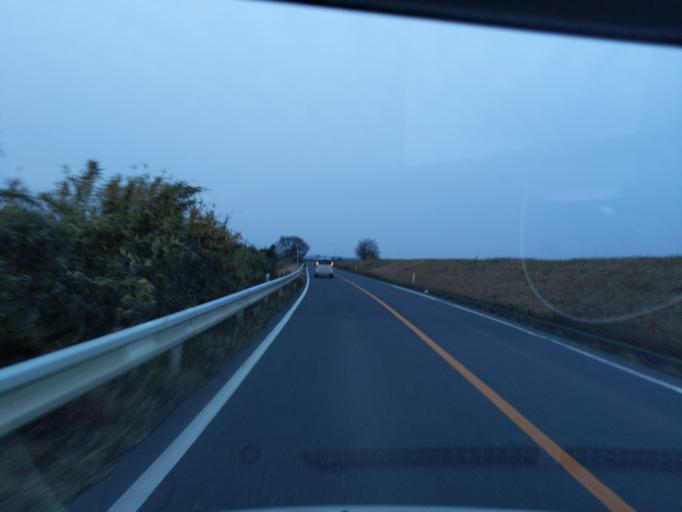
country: JP
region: Iwate
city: Ichinoseki
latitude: 38.7396
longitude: 141.1518
